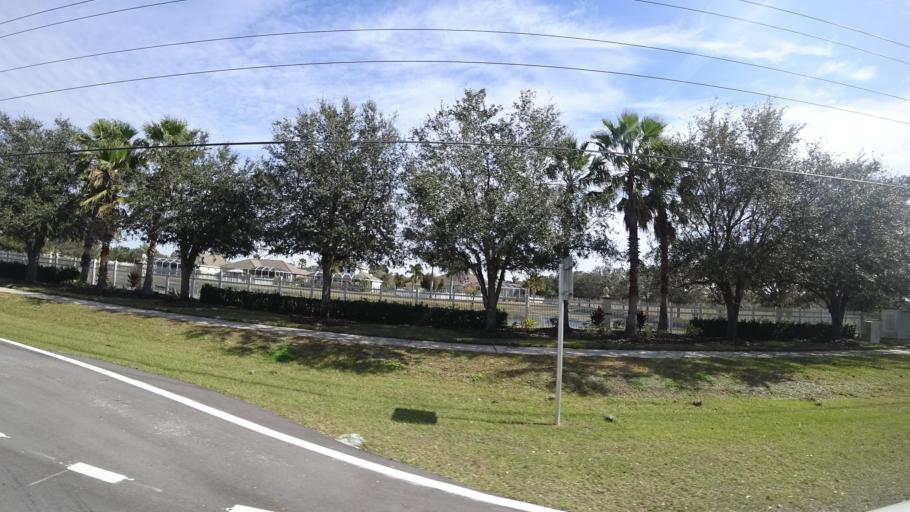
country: US
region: Florida
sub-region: Manatee County
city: Ellenton
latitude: 27.5392
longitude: -82.4254
